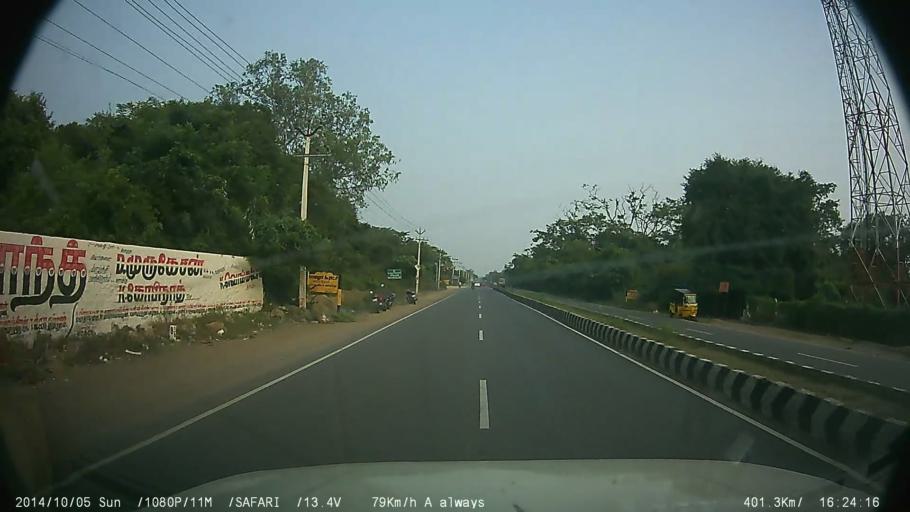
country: IN
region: Tamil Nadu
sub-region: Kancheepuram
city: Vengavasal
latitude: 12.8243
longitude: 80.1688
